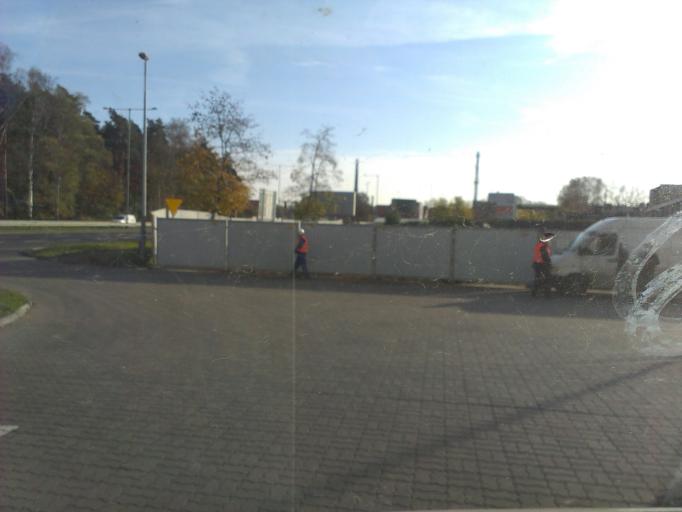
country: PL
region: West Pomeranian Voivodeship
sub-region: Powiat gryfinski
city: Stare Czarnowo
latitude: 53.3618
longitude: 14.7418
